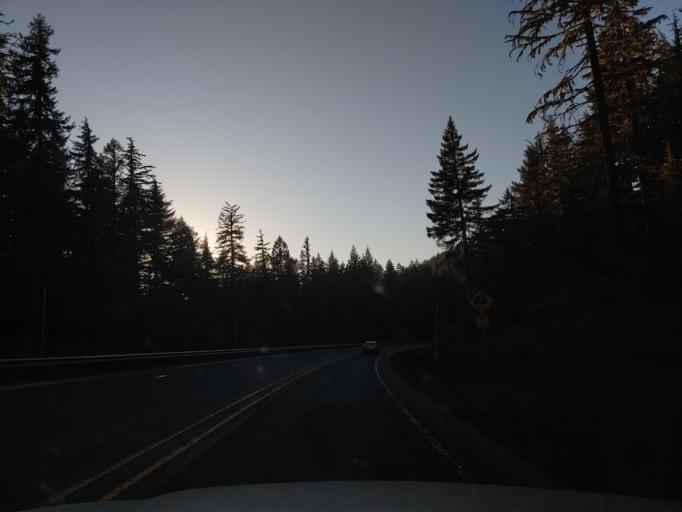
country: US
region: Oregon
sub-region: Lane County
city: Oakridge
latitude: 43.6111
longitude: -122.1234
